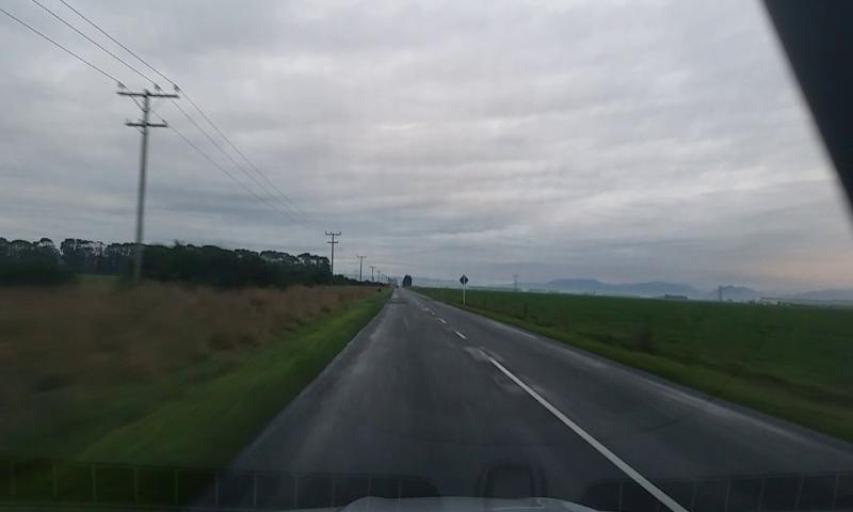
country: NZ
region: Canterbury
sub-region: Ashburton District
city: Rakaia
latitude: -43.7526
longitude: 171.8608
